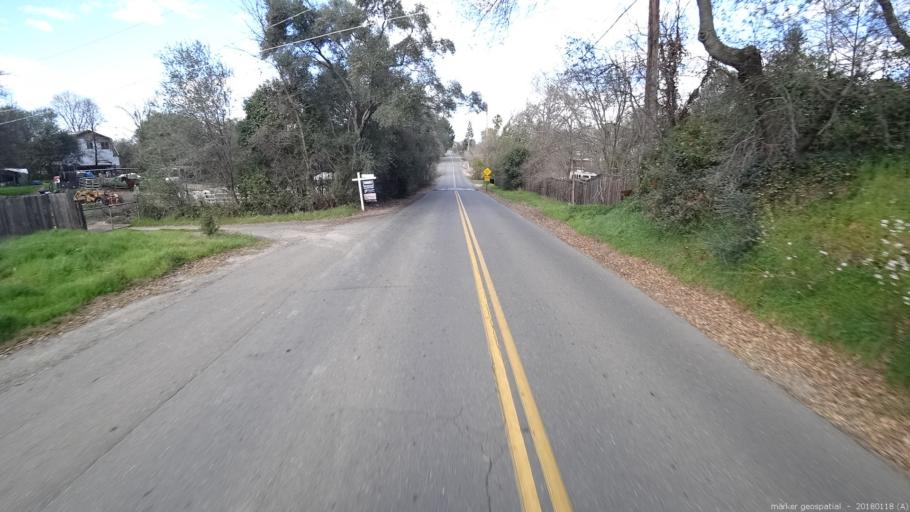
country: US
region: California
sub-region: Sacramento County
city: Orangevale
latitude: 38.6944
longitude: -121.2064
